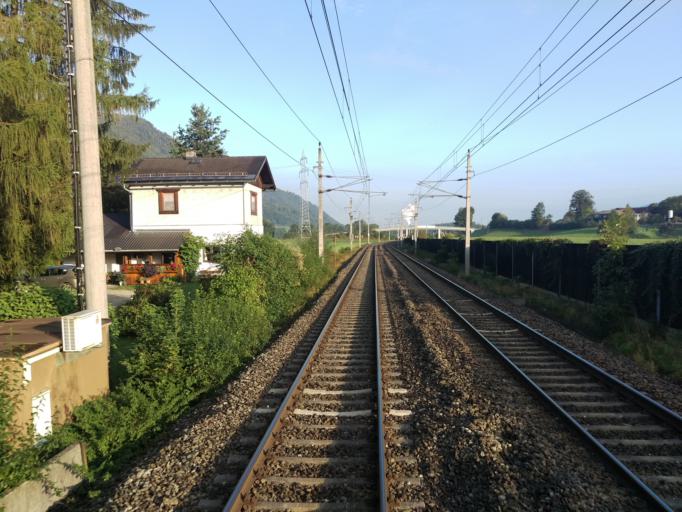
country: AT
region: Salzburg
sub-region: Politischer Bezirk Hallein
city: Kuchl
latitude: 47.6415
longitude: 13.1335
